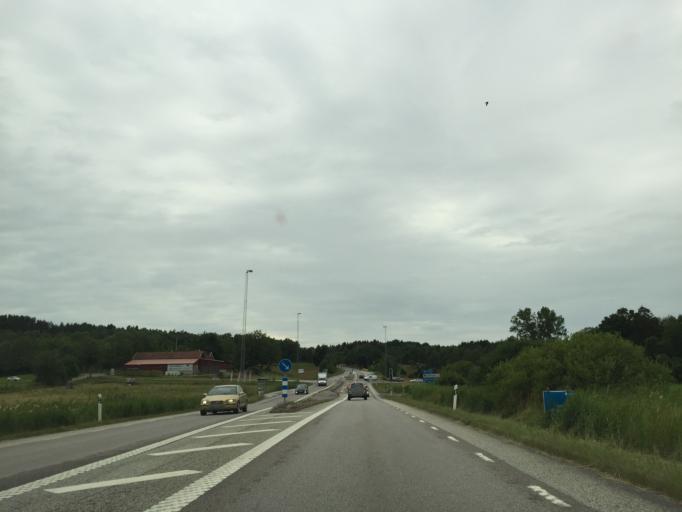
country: SE
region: Vaestra Goetaland
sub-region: Tjorns Kommun
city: Myggenas
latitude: 58.0240
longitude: 11.6983
